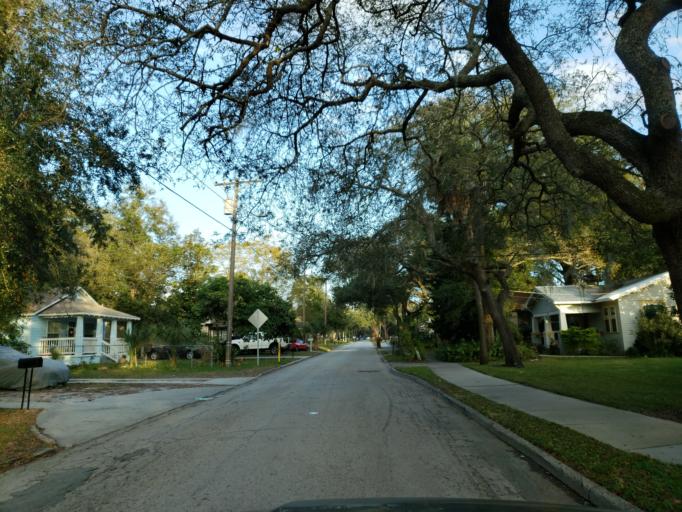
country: US
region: Florida
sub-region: Hillsborough County
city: Tampa
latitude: 27.9952
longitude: -82.4469
